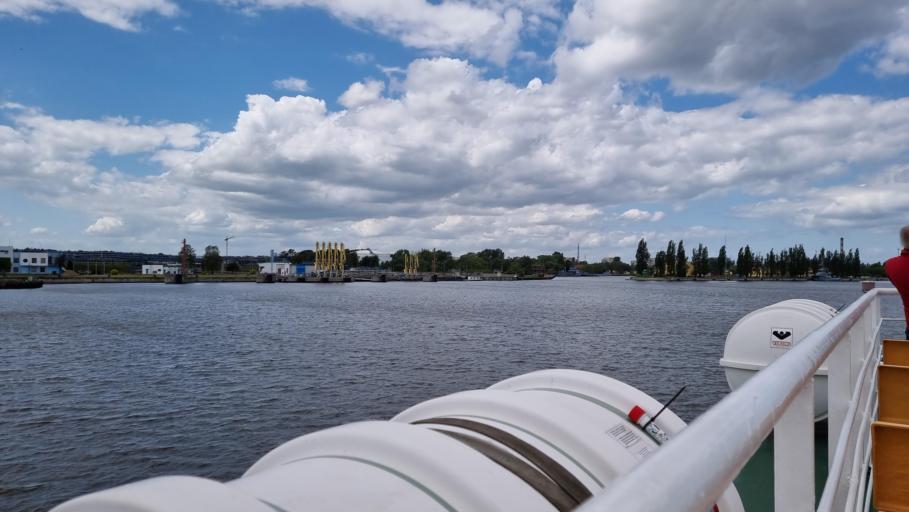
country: PL
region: West Pomeranian Voivodeship
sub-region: Swinoujscie
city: Swinoujscie
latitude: 53.8932
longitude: 14.2556
